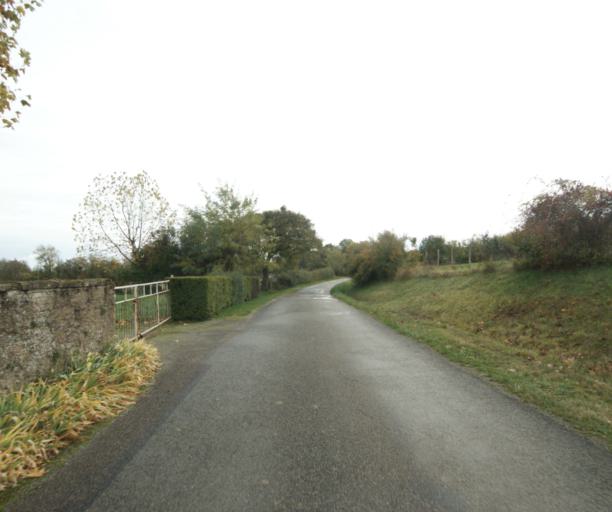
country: FR
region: Rhone-Alpes
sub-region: Departement de l'Ain
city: Pont-de-Vaux
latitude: 46.4737
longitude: 4.8769
